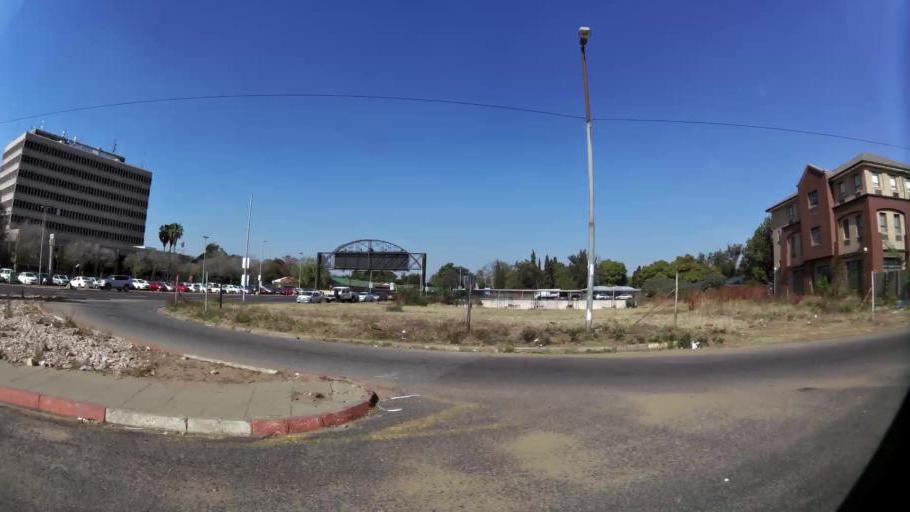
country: ZA
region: North-West
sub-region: Bojanala Platinum District Municipality
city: Rustenburg
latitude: -25.6731
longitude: 27.2430
